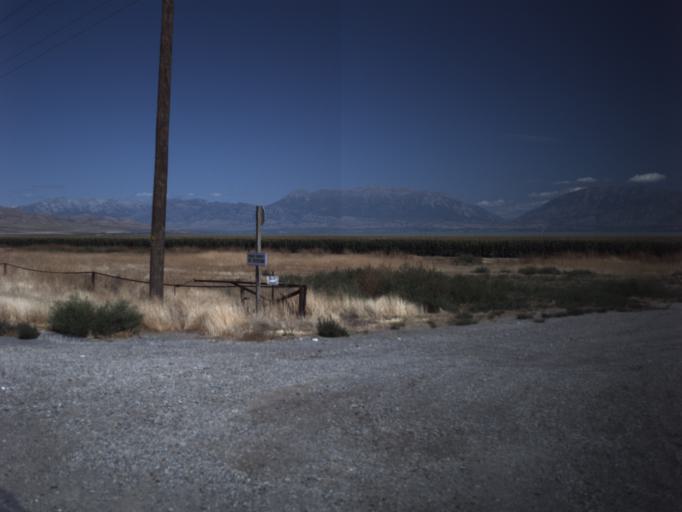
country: US
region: Utah
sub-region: Utah County
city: Genola
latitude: 40.0933
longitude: -111.9589
